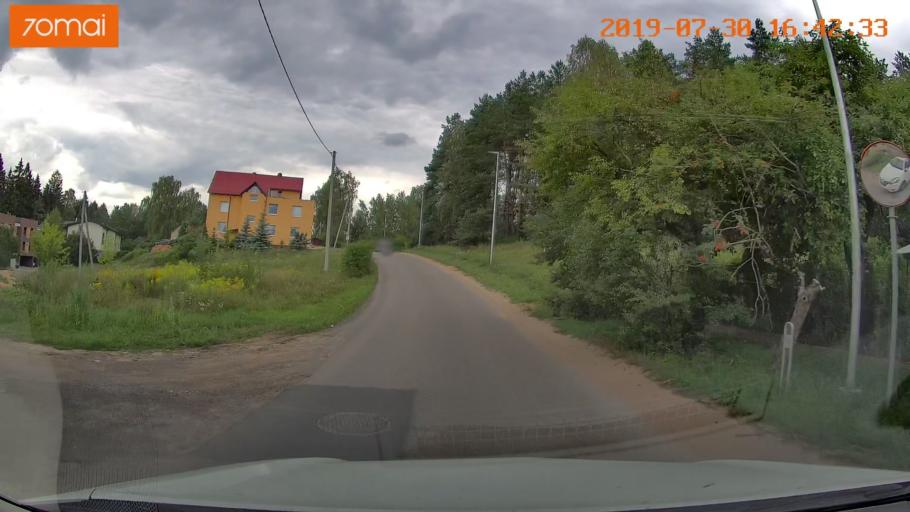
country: LT
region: Vilnius County
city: Rasos
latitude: 54.7164
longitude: 25.3537
